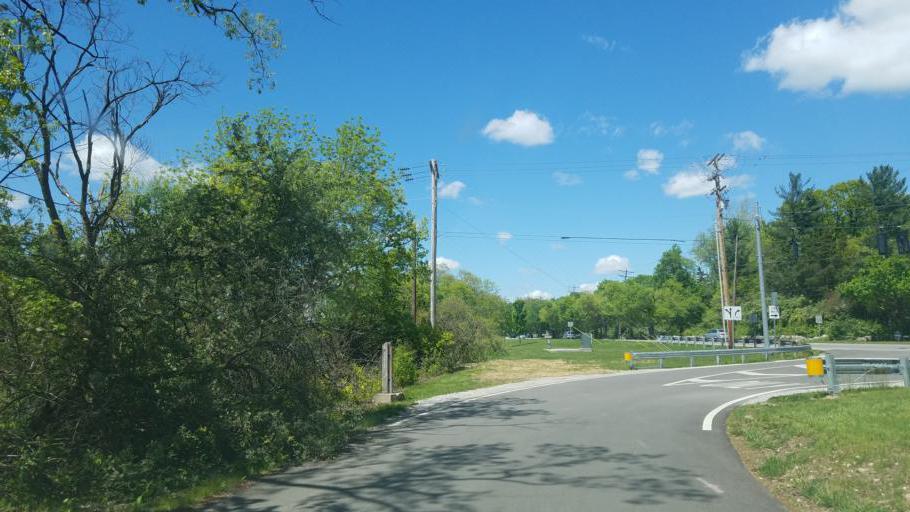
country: US
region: Ohio
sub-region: Franklin County
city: Dublin
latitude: 40.0474
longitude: -83.0955
